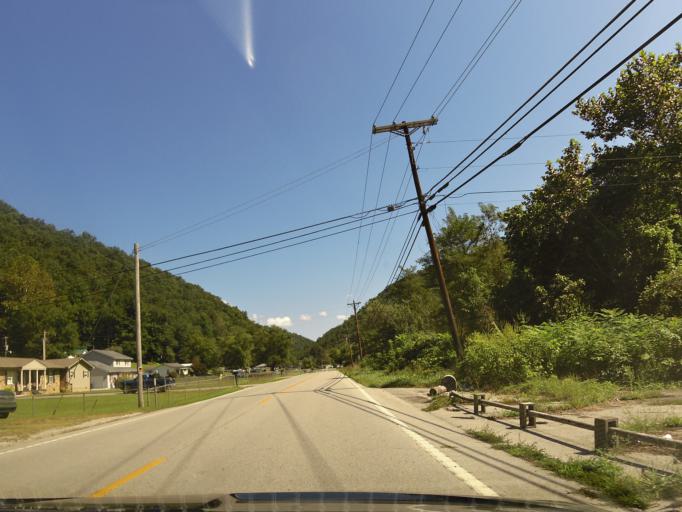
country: US
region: Kentucky
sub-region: Clay County
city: Manchester
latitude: 37.1412
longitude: -83.6104
